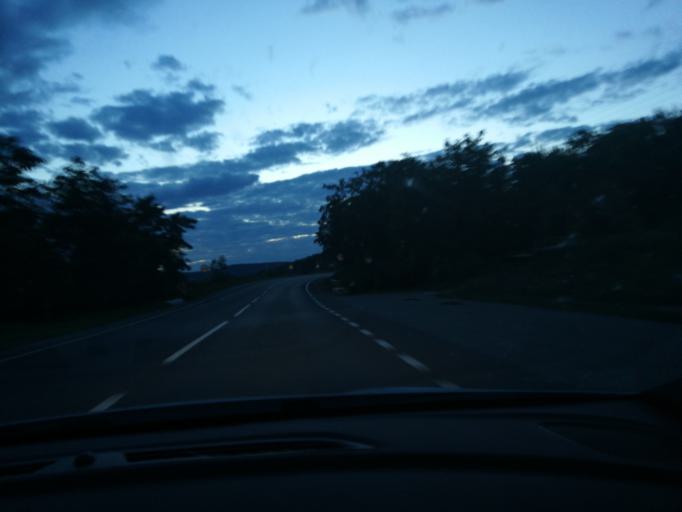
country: RO
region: Mures
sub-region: Comuna Saschiz
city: Saschiz
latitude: 46.1573
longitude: 25.0146
